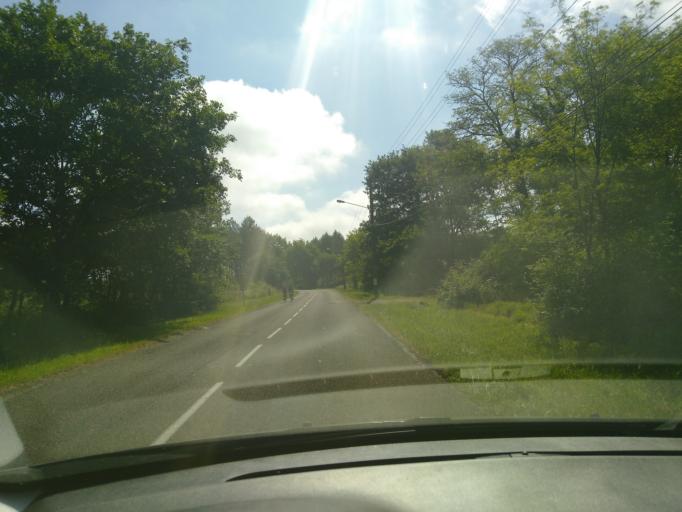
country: FR
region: Aquitaine
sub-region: Departement des Landes
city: Saint-Vincent-de-Paul
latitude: 43.7844
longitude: -0.9849
